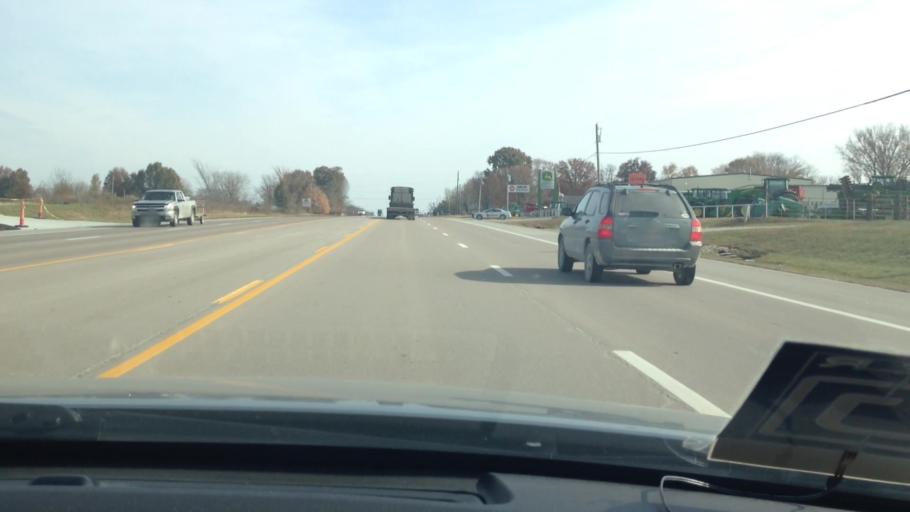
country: US
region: Missouri
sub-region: Henry County
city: Clinton
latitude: 38.3896
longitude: -93.8104
